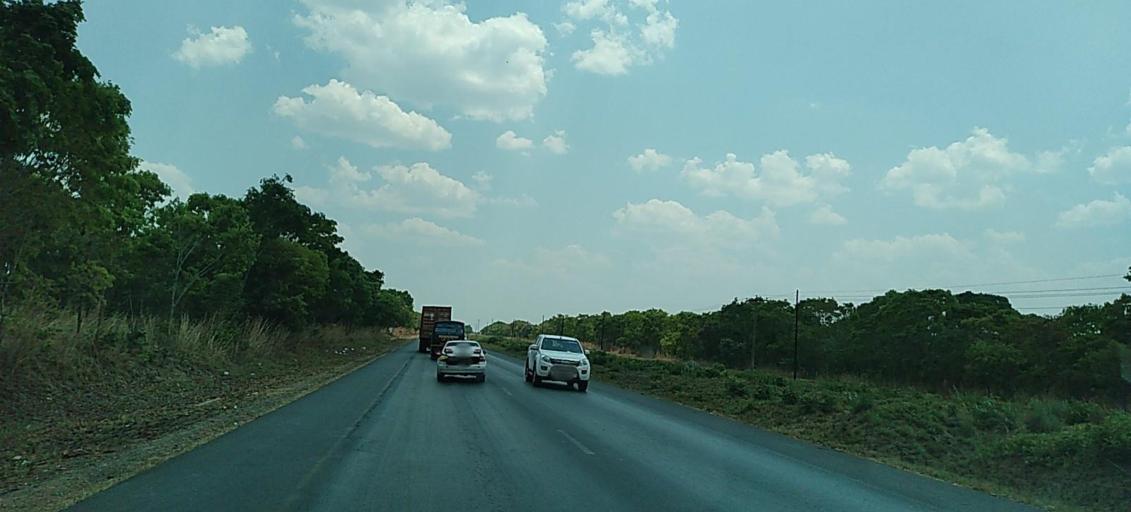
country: ZM
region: Central
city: Kabwe
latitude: -14.3307
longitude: 28.5370
